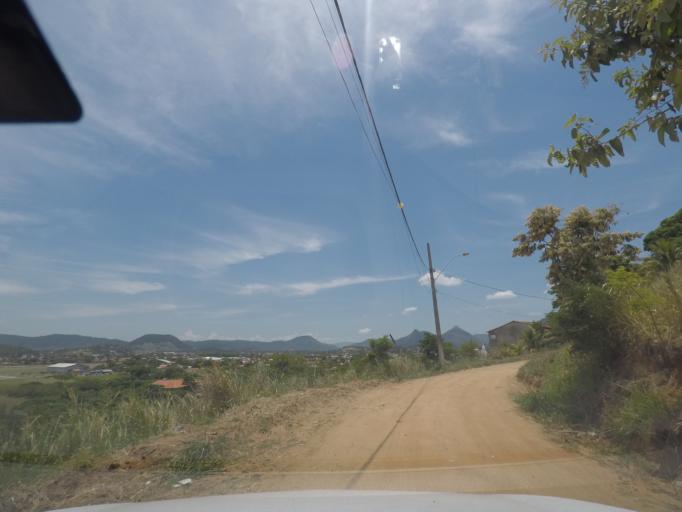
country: BR
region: Rio de Janeiro
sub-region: Marica
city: Marica
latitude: -22.9248
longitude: -42.8273
